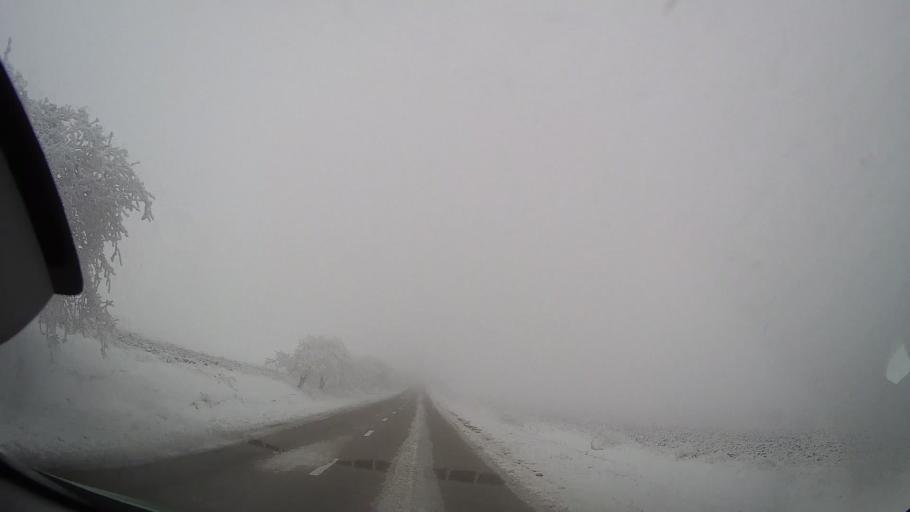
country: RO
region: Neamt
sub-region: Comuna Valea Ursului
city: Valea Ursului
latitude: 46.8287
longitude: 27.0646
